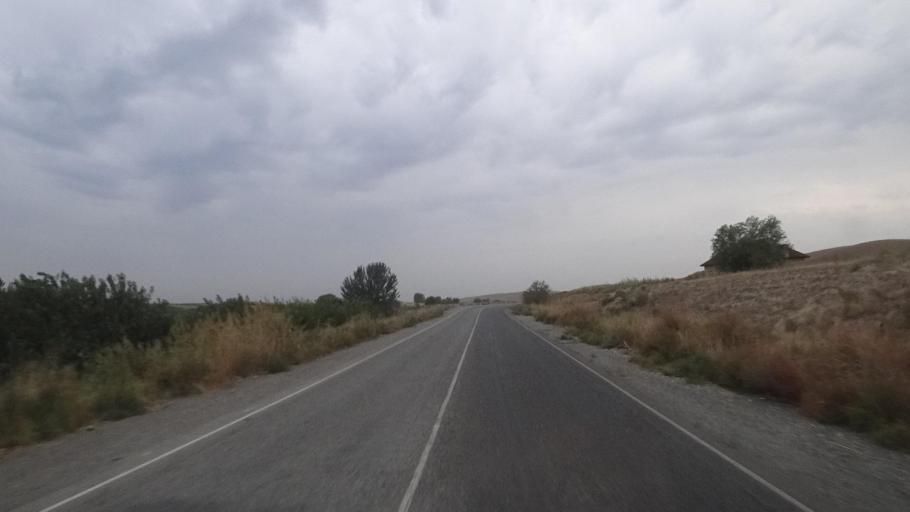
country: UZ
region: Namangan
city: Uchqurghon Shahri
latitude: 41.0521
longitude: 72.2607
